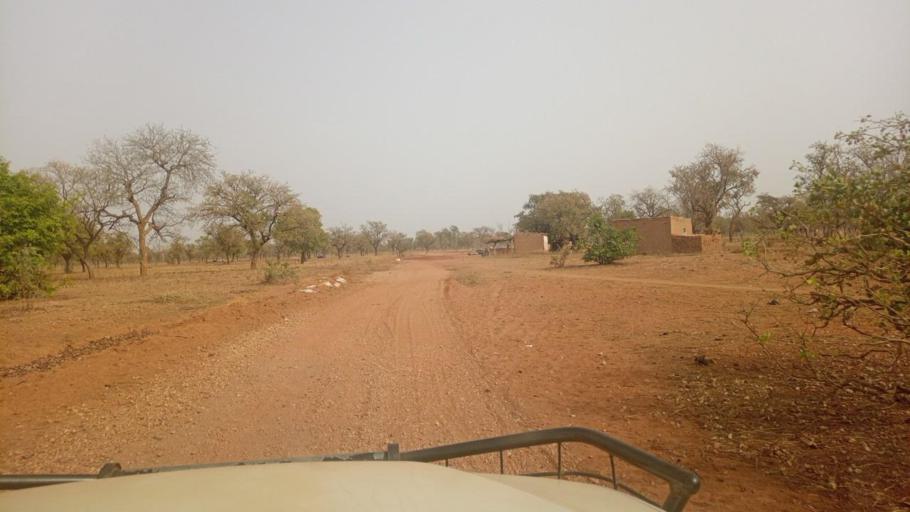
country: BF
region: Boucle du Mouhoun
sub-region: Province des Banwa
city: Salanso
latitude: 12.0946
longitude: -4.3296
